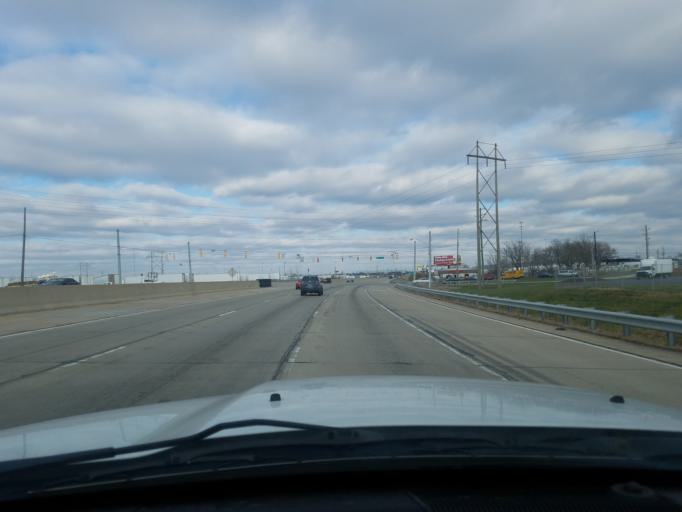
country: US
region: Indiana
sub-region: Marion County
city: Southport
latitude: 39.6850
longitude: -86.1944
